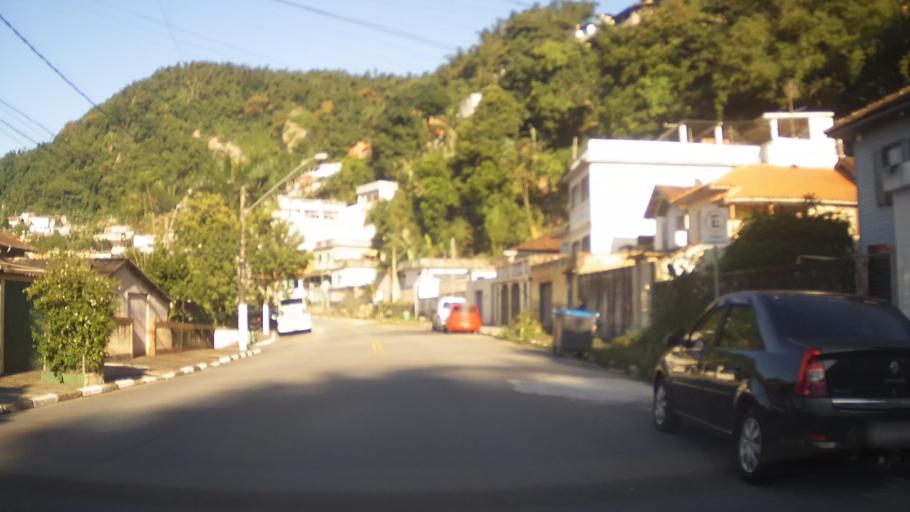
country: BR
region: Sao Paulo
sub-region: Santos
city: Santos
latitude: -23.9400
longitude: -46.3400
